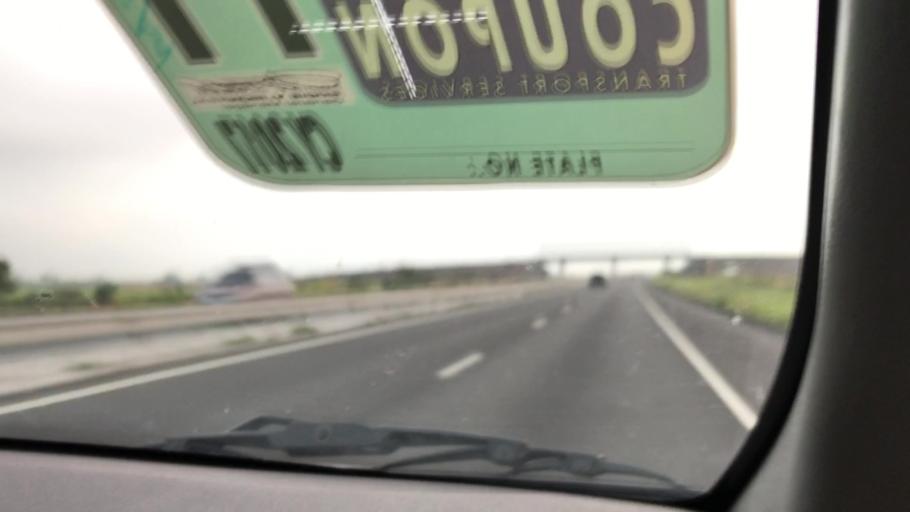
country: PH
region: Central Luzon
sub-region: Province of Tarlac
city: Mapalacsiao
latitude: 15.4206
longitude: 120.6616
